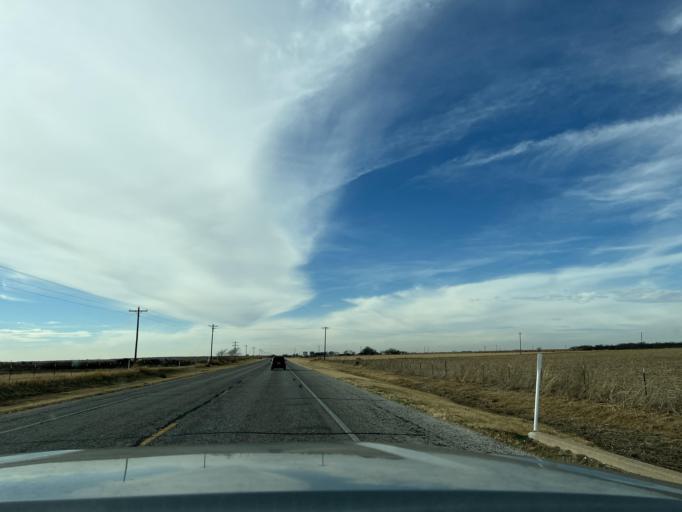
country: US
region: Texas
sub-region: Fisher County
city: Roby
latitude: 32.7560
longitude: -100.2722
